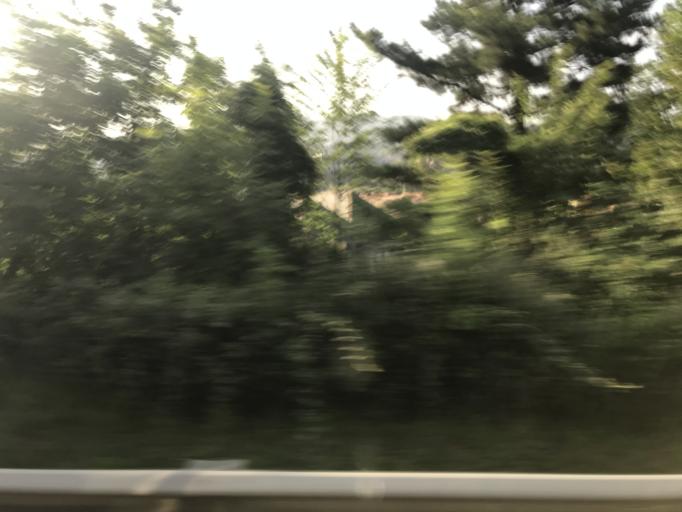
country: ES
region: Basque Country
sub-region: Provincia de Guipuzcoa
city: Idiazabal
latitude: 43.0244
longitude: -2.2321
